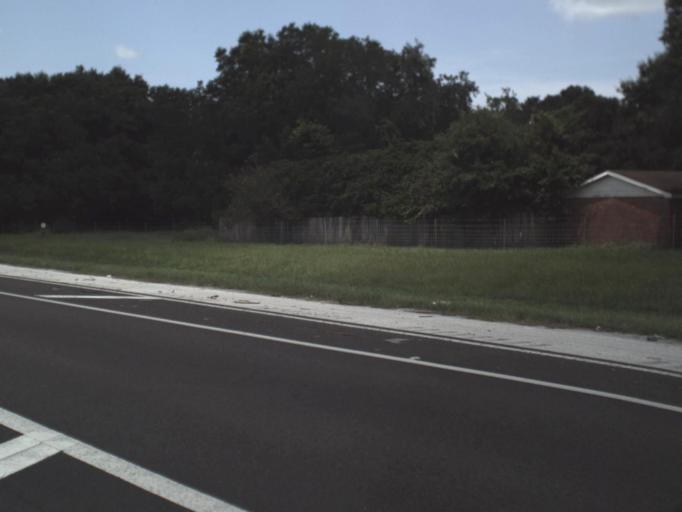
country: US
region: Florida
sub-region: Hillsborough County
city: Plant City
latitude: 28.0273
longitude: -82.1602
